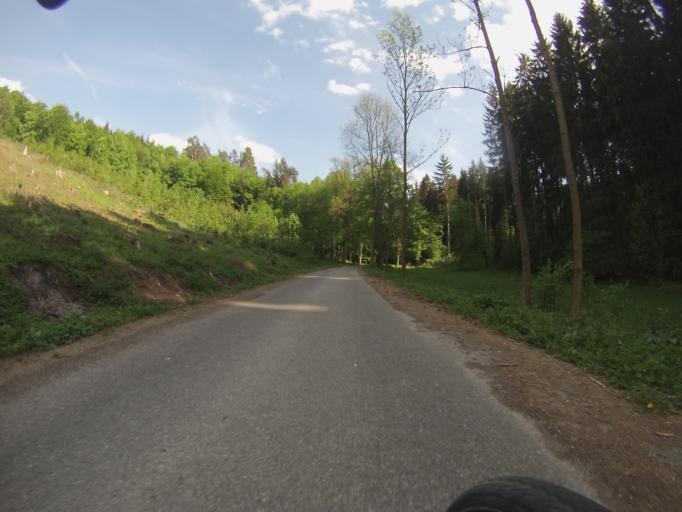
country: CZ
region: South Moravian
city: Ostrov u Macochy
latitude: 49.4026
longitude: 16.7369
